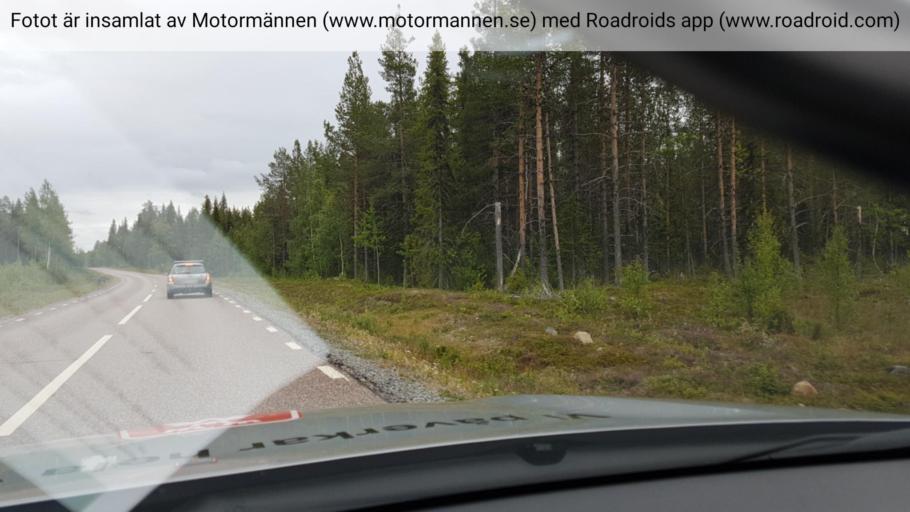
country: SE
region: Norrbotten
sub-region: Gallivare Kommun
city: Gaellivare
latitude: 67.0560
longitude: 21.5869
